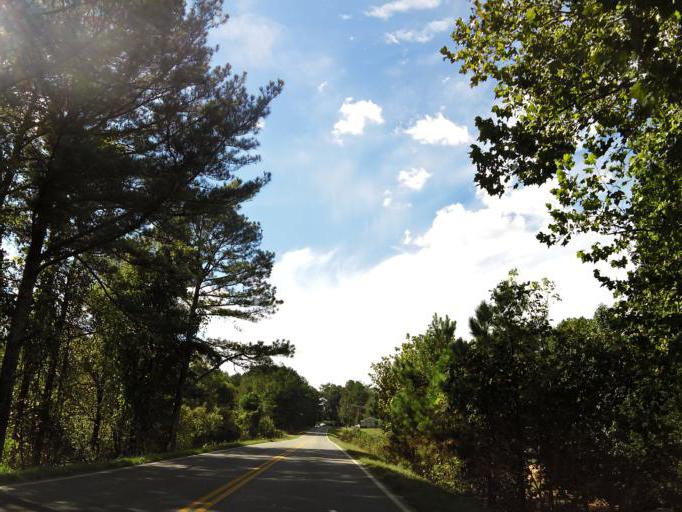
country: US
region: Georgia
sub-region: Pickens County
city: Nelson
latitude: 34.4103
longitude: -84.4053
